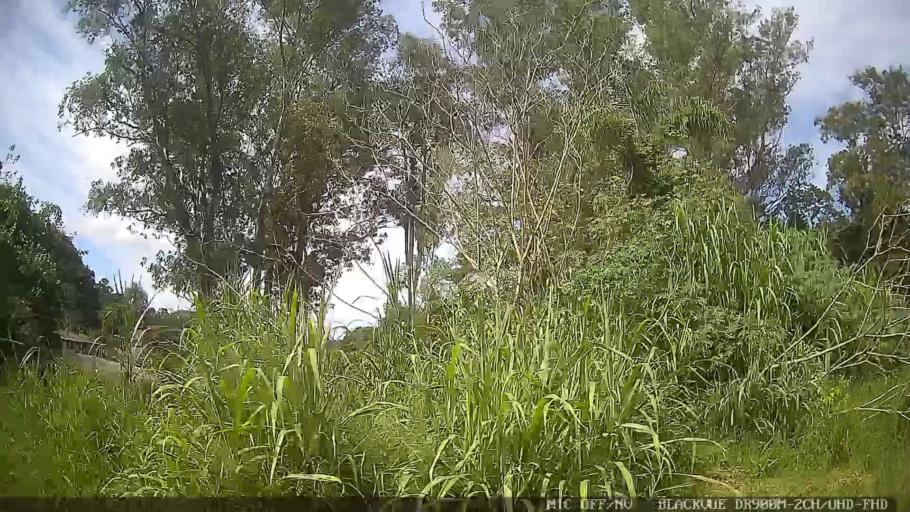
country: BR
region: Sao Paulo
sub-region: Jarinu
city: Jarinu
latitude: -23.0427
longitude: -46.6425
